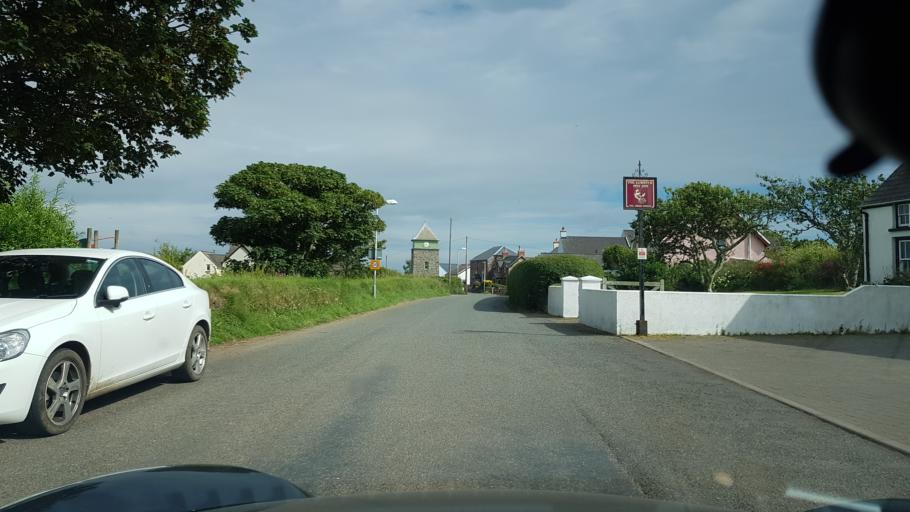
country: GB
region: Wales
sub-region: Pembrokeshire
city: Dale
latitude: 51.7317
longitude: -5.1979
